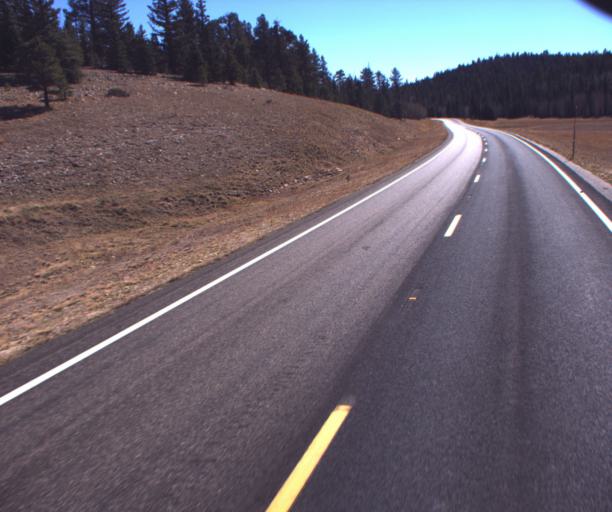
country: US
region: Arizona
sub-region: Coconino County
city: Grand Canyon
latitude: 36.5289
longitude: -112.1500
